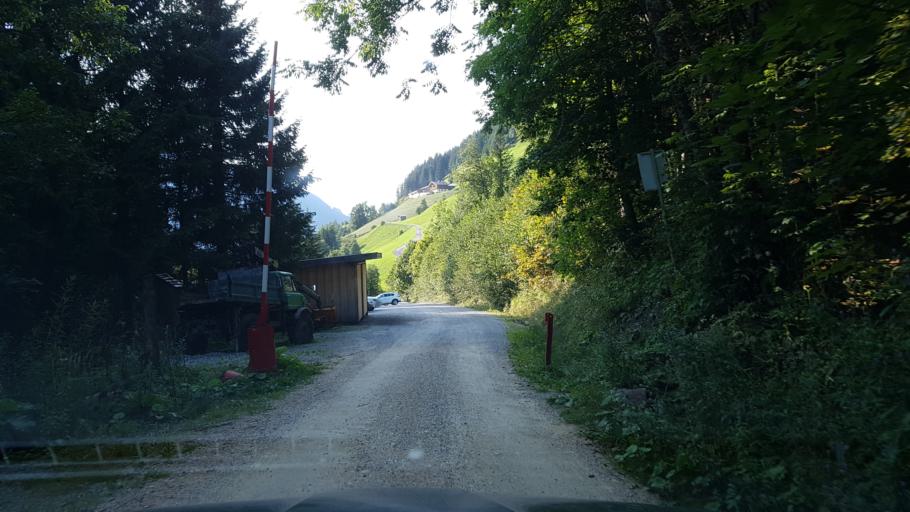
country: AT
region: Salzburg
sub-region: Politischer Bezirk Sankt Johann im Pongau
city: Kleinarl
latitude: 47.2742
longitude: 13.2459
